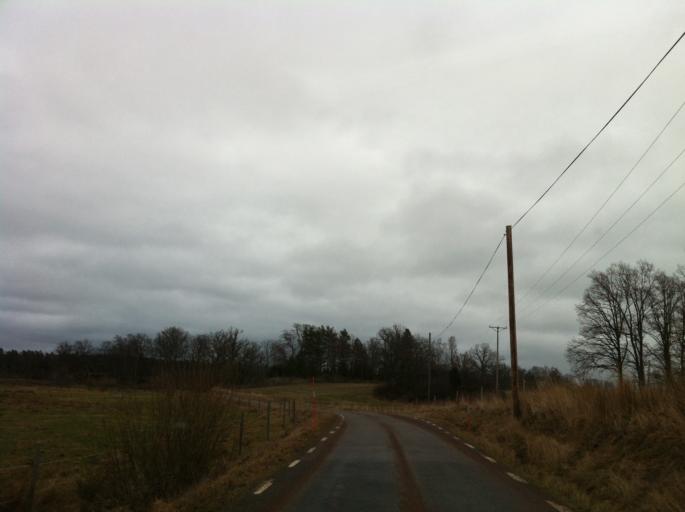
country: SE
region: Kalmar
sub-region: Vasterviks Kommun
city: Vaestervik
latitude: 57.9156
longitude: 16.6281
